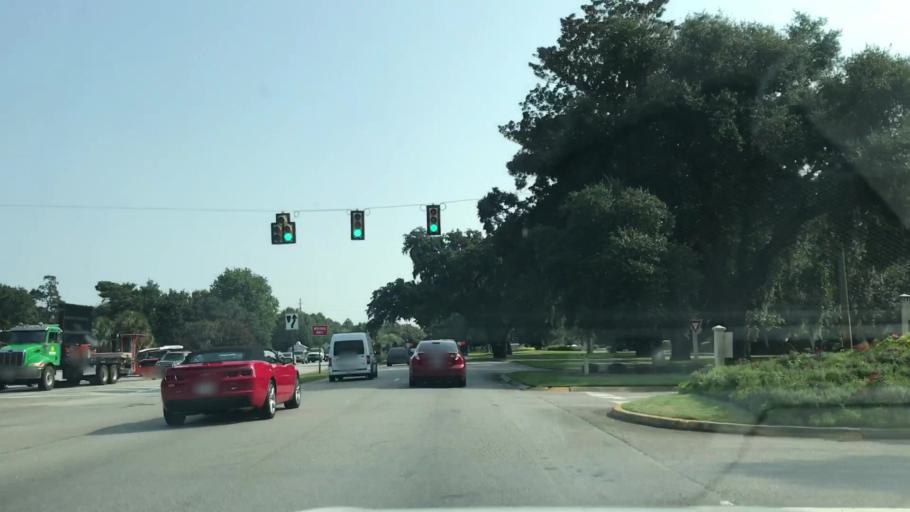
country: US
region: South Carolina
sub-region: Georgetown County
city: Murrells Inlet
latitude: 33.4836
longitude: -79.0963
